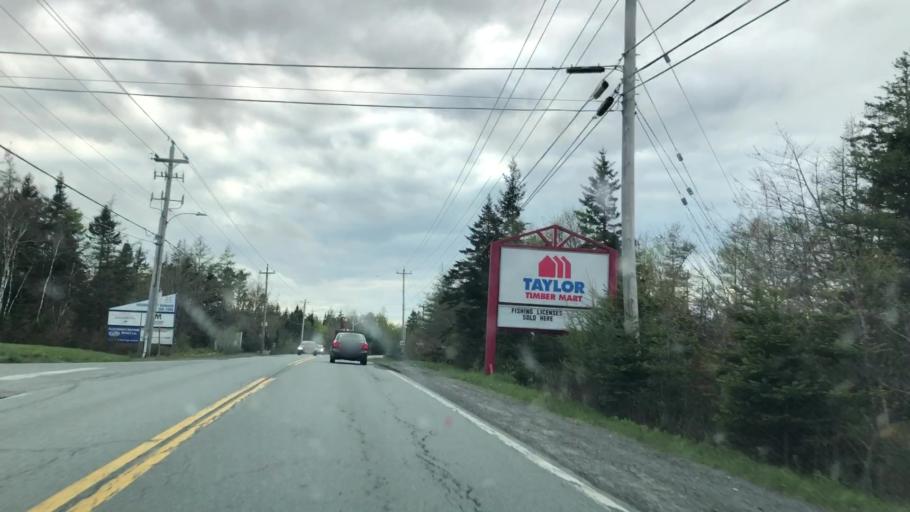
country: CA
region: Nova Scotia
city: Cole Harbour
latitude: 44.7824
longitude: -63.1730
